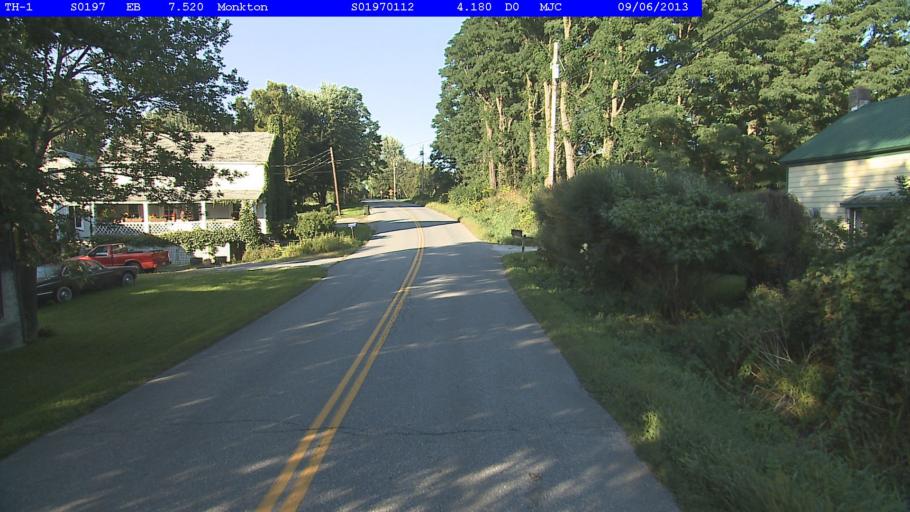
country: US
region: Vermont
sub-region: Chittenden County
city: Hinesburg
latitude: 44.2352
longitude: -73.1460
